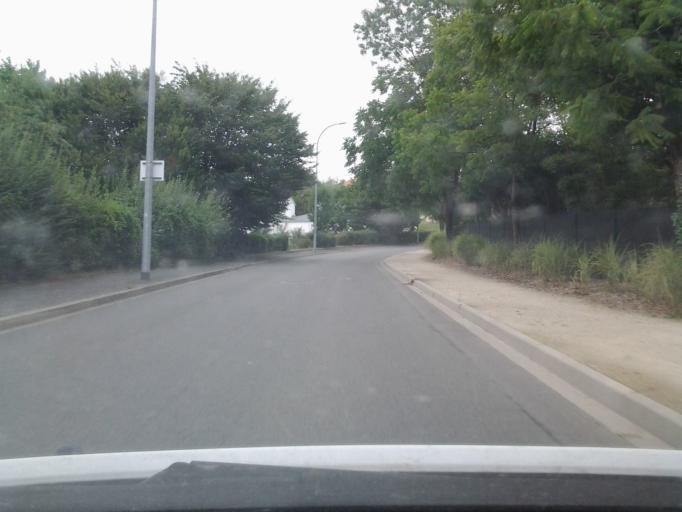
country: FR
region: Pays de la Loire
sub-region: Departement de la Vendee
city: La Roche-sur-Yon
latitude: 46.6553
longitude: -1.4239
